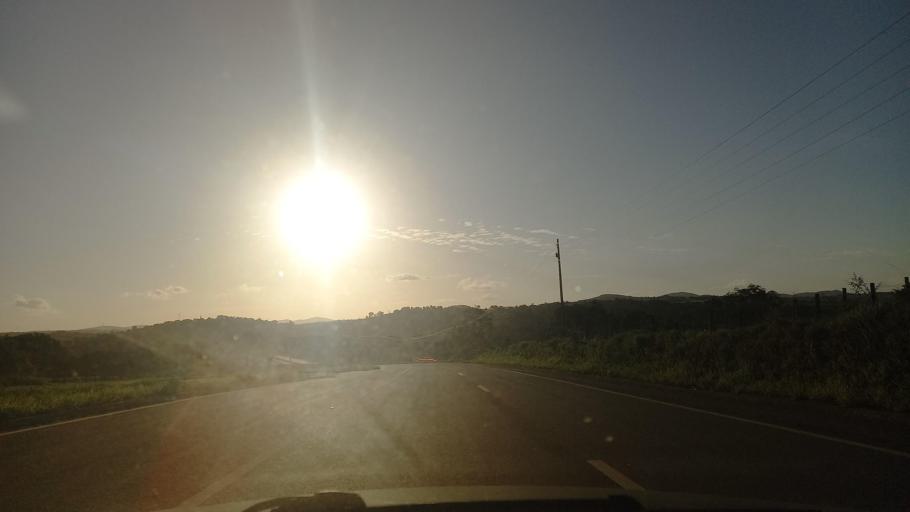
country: BR
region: Alagoas
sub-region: Limoeiro De Anadia
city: Limoeiro de Anadia
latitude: -9.7391
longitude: -36.4849
